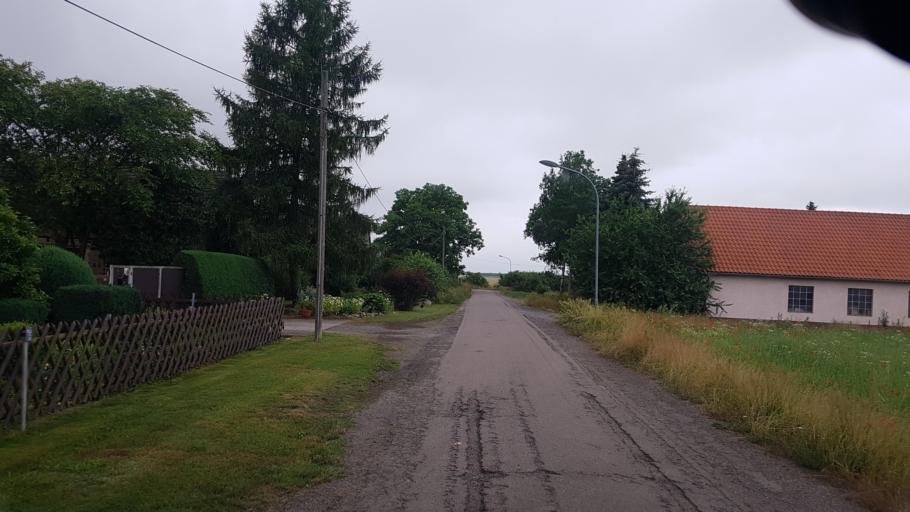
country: DE
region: Brandenburg
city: Juterbog
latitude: 51.9100
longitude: 13.1929
